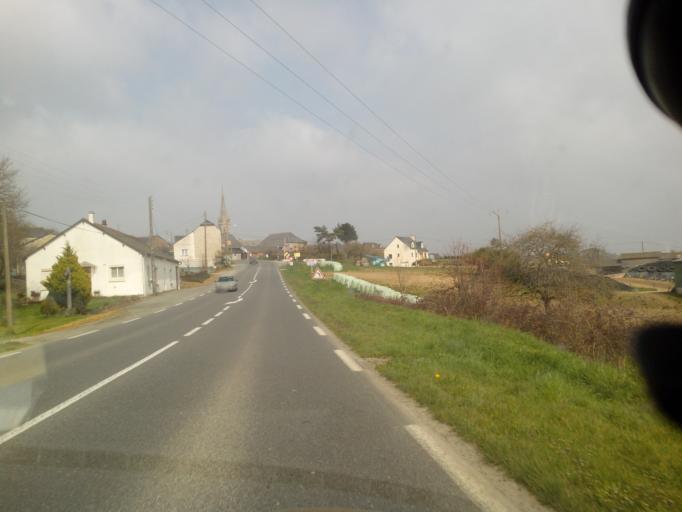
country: FR
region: Brittany
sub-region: Departement des Cotes-d'Armor
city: Caulnes
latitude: 48.2649
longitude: -2.1610
